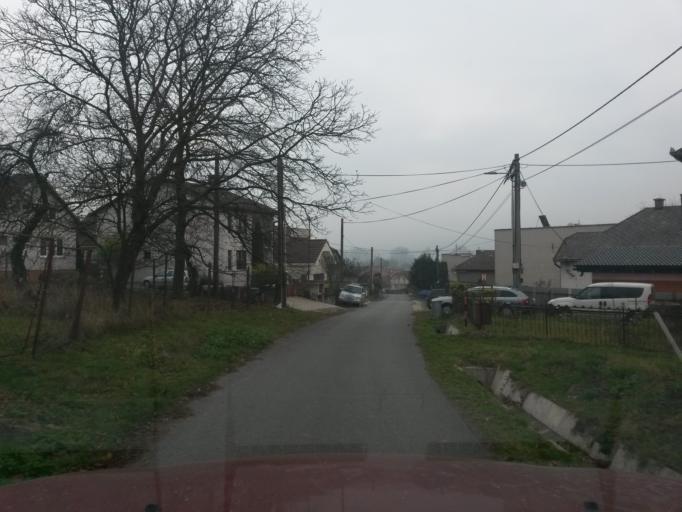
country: SK
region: Presovsky
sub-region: Okres Presov
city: Presov
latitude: 48.8764
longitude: 21.2683
